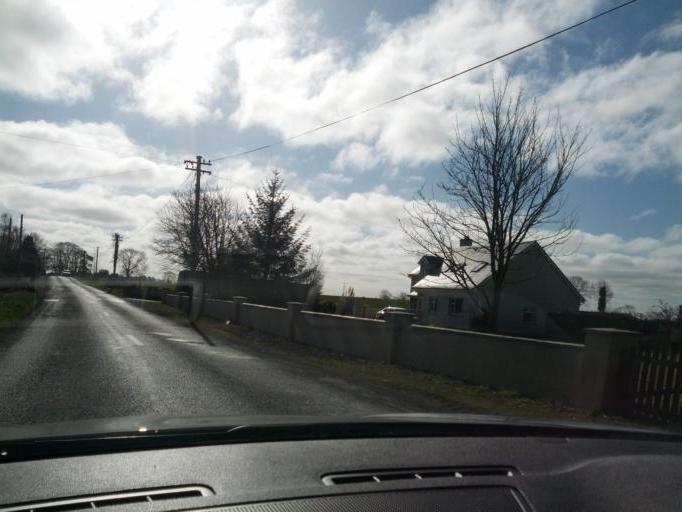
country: IE
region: Connaught
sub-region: County Galway
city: Ballinasloe
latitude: 53.3695
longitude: -8.2650
